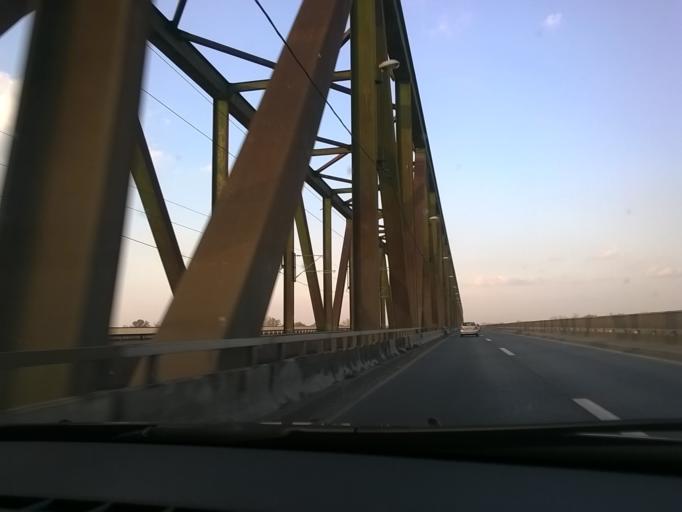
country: RS
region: Central Serbia
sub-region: Belgrade
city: Palilula
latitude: 44.8267
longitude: 20.4917
